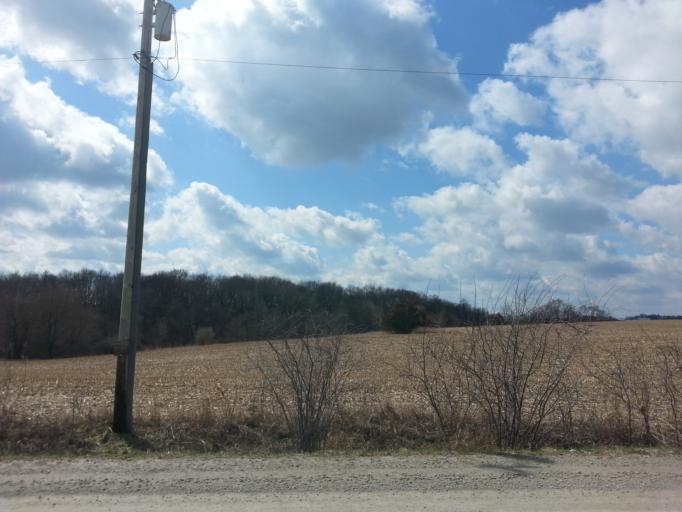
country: US
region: Minnesota
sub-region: Dodge County
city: Mantorville
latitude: 44.0706
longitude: -92.7183
